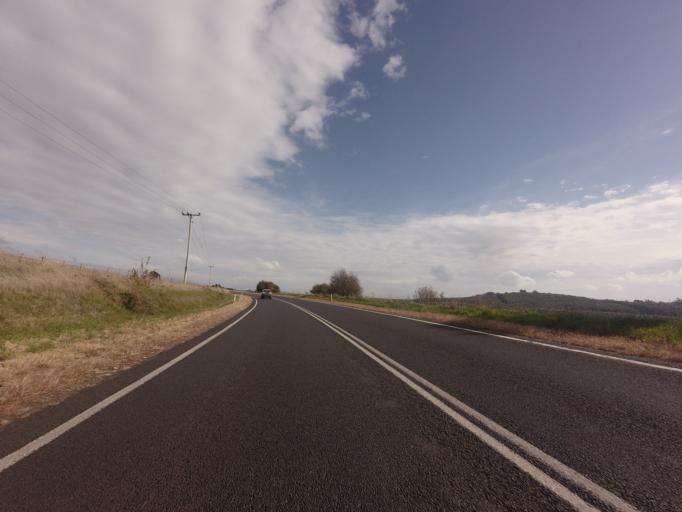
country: AU
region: Tasmania
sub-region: Meander Valley
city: Deloraine
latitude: -41.5179
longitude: 146.7240
